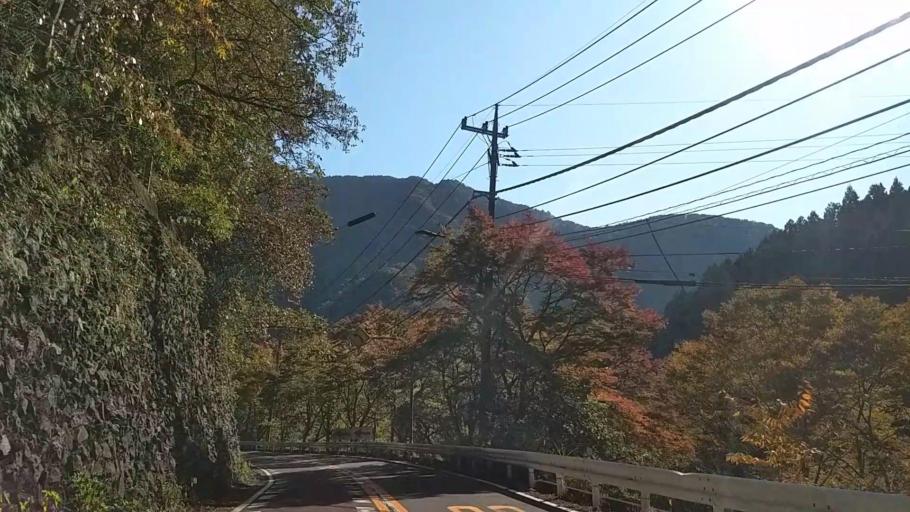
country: JP
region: Tokyo
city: Itsukaichi
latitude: 35.7939
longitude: 139.0578
